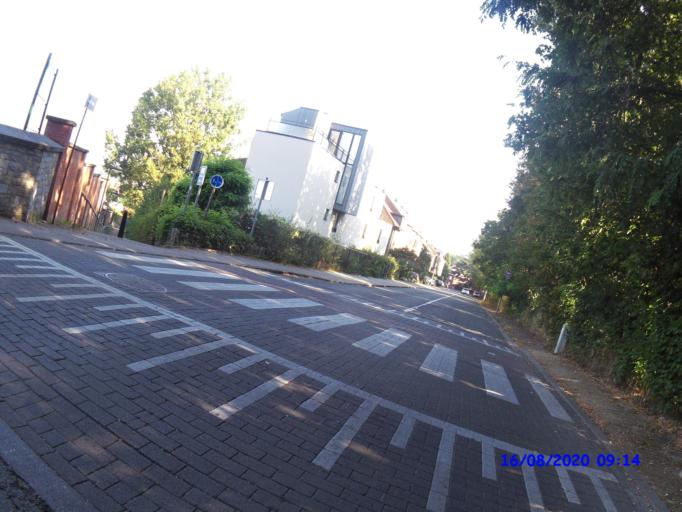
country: BE
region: Flanders
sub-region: Provincie Vlaams-Brabant
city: Linkebeek
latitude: 50.7819
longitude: 4.3328
